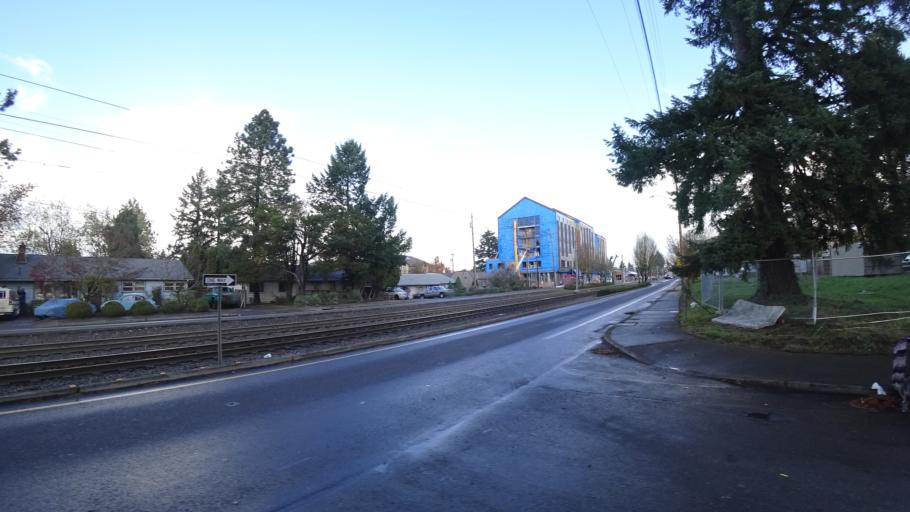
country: US
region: Oregon
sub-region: Multnomah County
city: Lents
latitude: 45.5224
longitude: -122.5405
